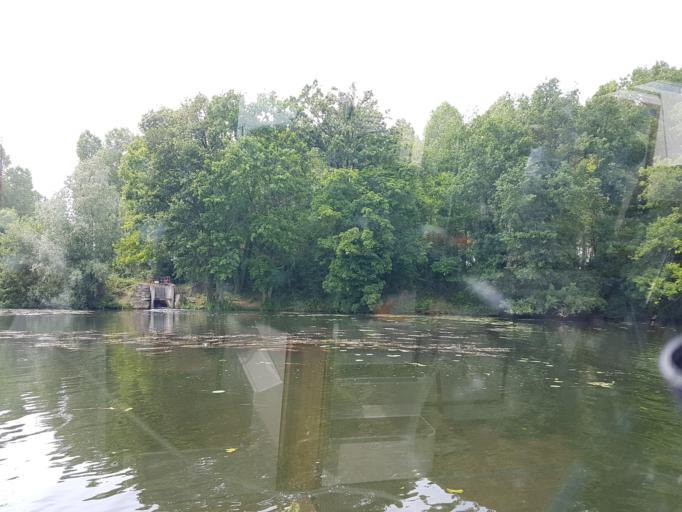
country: FR
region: Bourgogne
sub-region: Departement de l'Yonne
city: Gurgy
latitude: 47.8630
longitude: 3.5524
